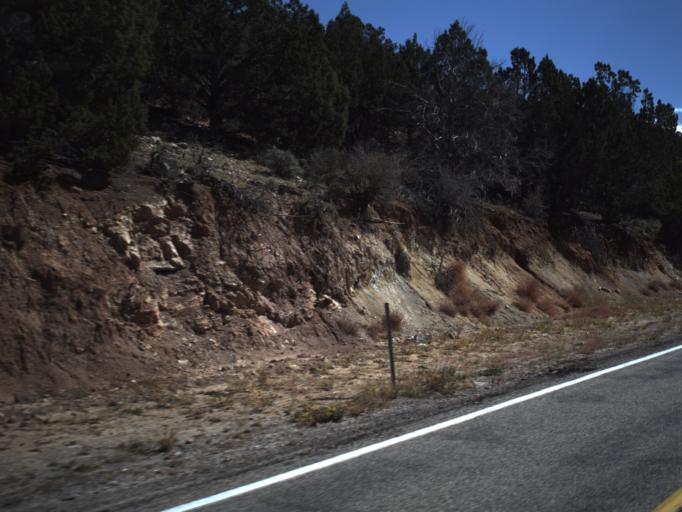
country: US
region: Utah
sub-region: Washington County
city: Enterprise
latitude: 37.5445
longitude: -113.6844
